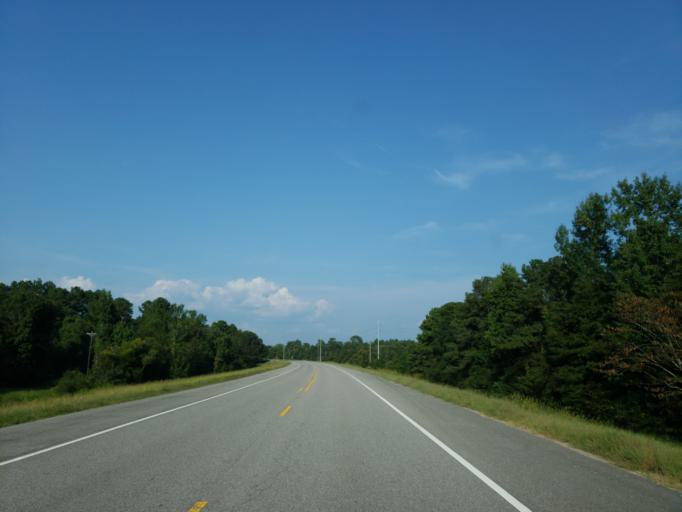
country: US
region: Alabama
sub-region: Sumter County
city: Livingston
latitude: 32.6993
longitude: -88.0945
